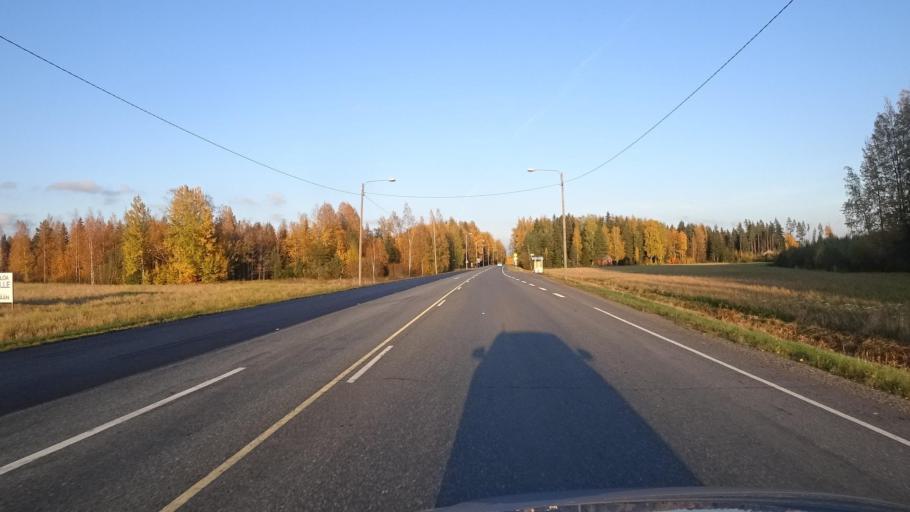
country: FI
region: Haeme
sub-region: Forssa
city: Ypaejae
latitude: 60.7723
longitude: 23.3455
